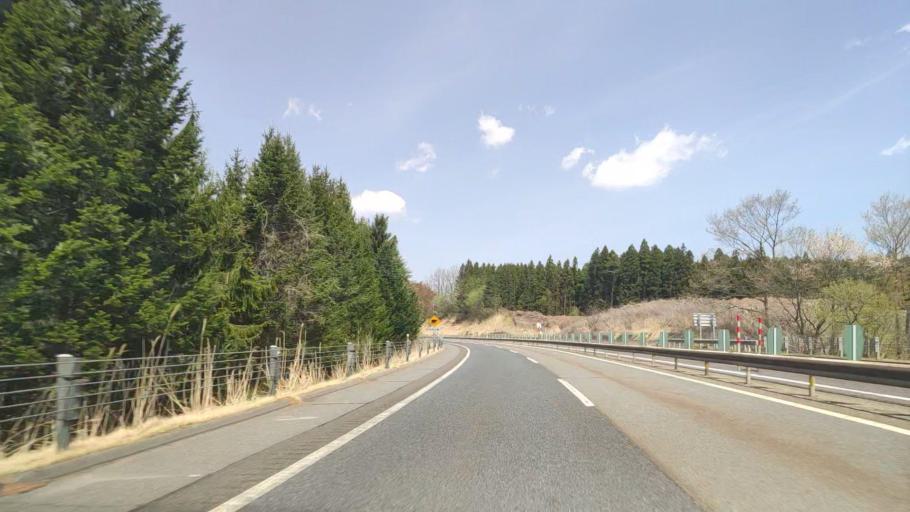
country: JP
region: Aomori
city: Hachinohe
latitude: 40.3947
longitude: 141.4482
